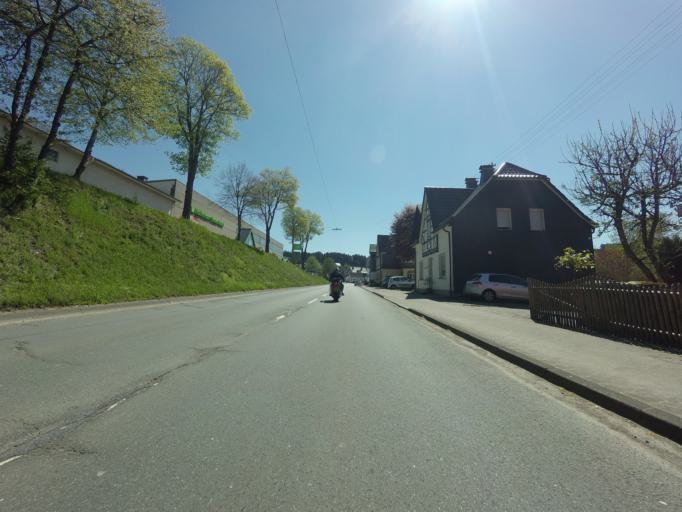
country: DE
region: North Rhine-Westphalia
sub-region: Regierungsbezirk Arnsberg
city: Kirchhundem
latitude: 51.0878
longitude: 8.1188
